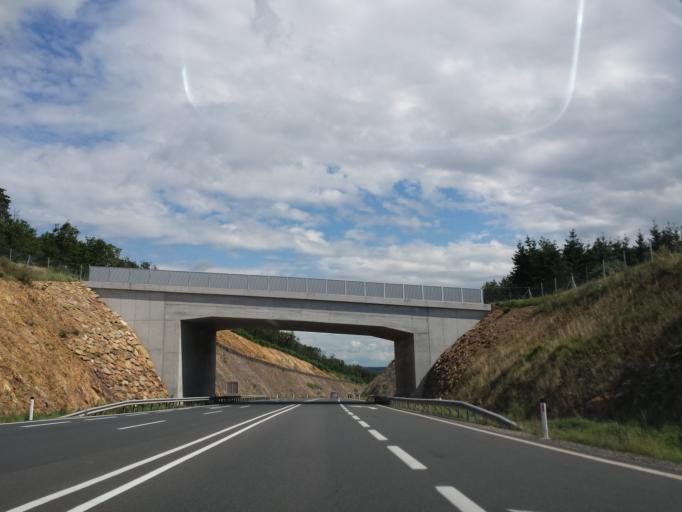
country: AT
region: Lower Austria
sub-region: Politischer Bezirk Hollabrunn
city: Maissau
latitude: 48.5824
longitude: 15.8296
